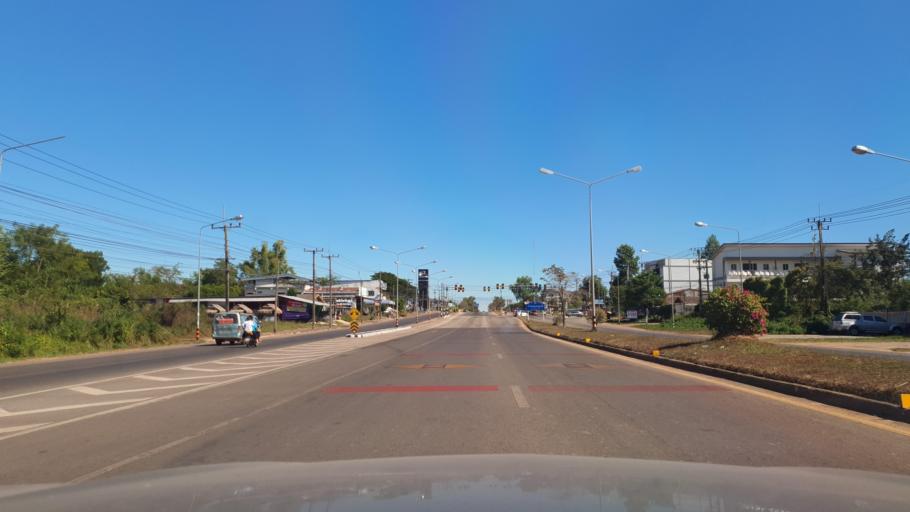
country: TH
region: Nakhon Phanom
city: Nakhon Phanom
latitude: 17.3833
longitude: 104.7352
